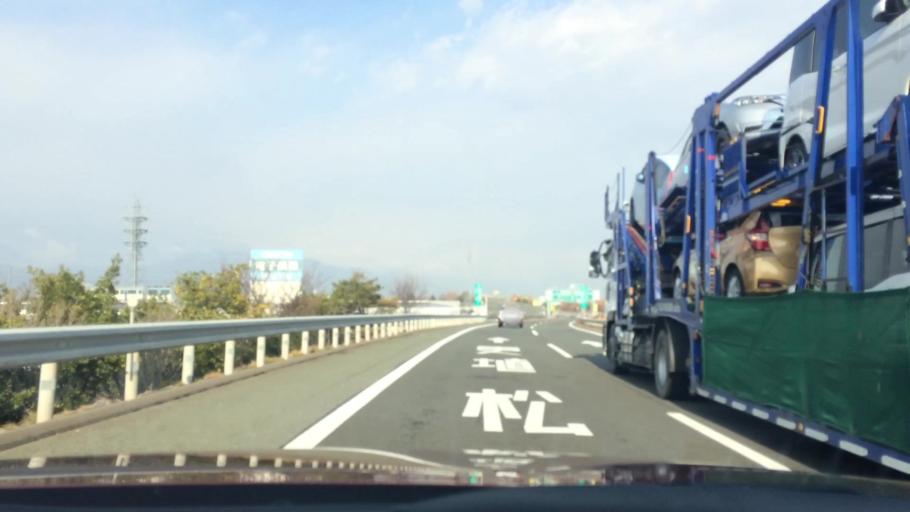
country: JP
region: Nagano
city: Nagano-shi
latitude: 36.5469
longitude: 138.1394
